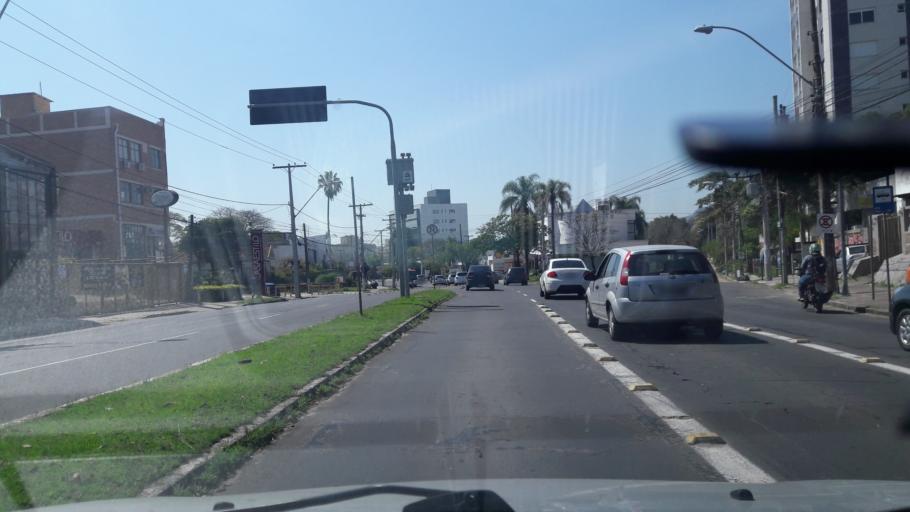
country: BR
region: Rio Grande do Sul
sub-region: Guaiba
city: Guaiba
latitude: -30.1036
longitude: -51.2523
